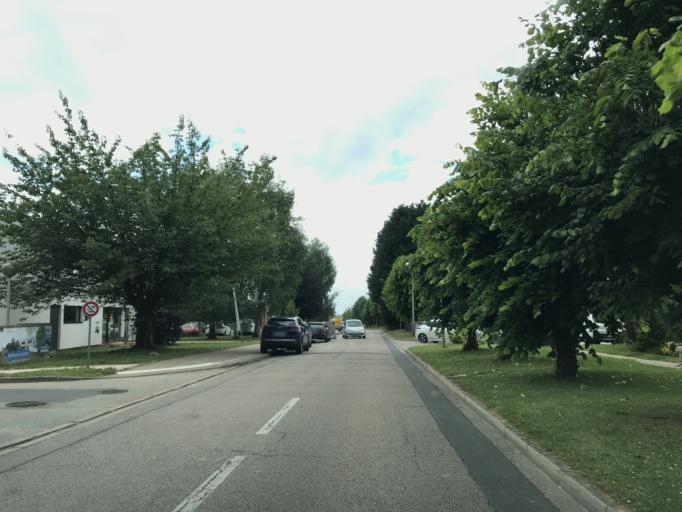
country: FR
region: Haute-Normandie
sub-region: Departement de la Seine-Maritime
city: Mont-Saint-Aignan
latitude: 49.4767
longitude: 1.0965
